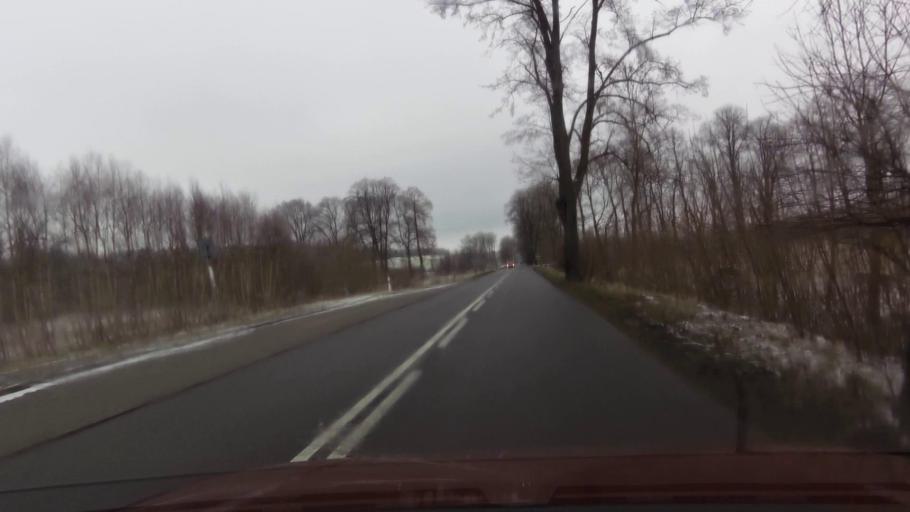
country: PL
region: West Pomeranian Voivodeship
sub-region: Powiat swidwinski
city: Polczyn-Zdroj
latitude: 53.7905
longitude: 16.0411
